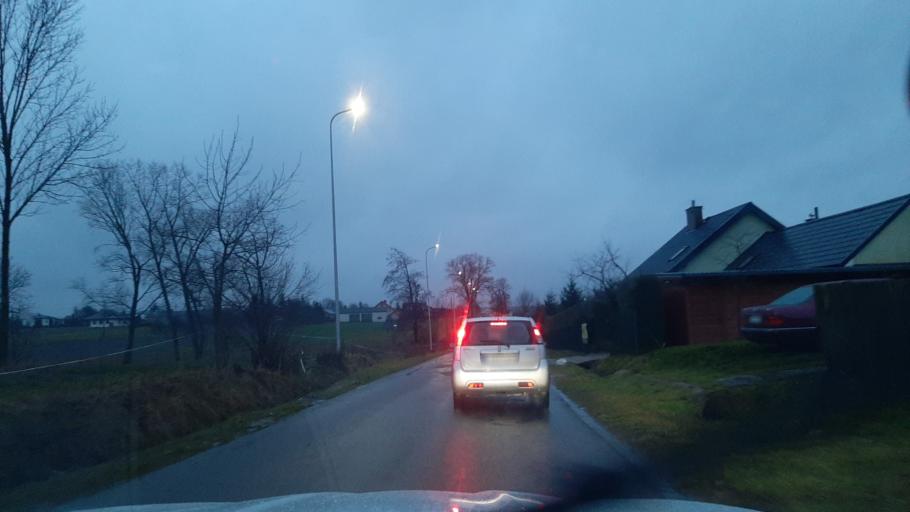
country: PL
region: Lublin Voivodeship
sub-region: Powiat lubelski
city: Jastkow
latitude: 51.3633
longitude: 22.4550
